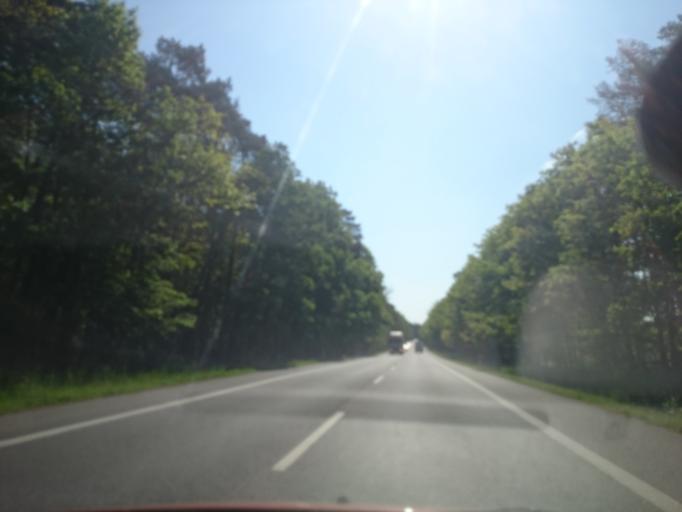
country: PL
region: Opole Voivodeship
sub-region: Powiat opolski
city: Chrzastowice
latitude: 50.6246
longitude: 18.0459
